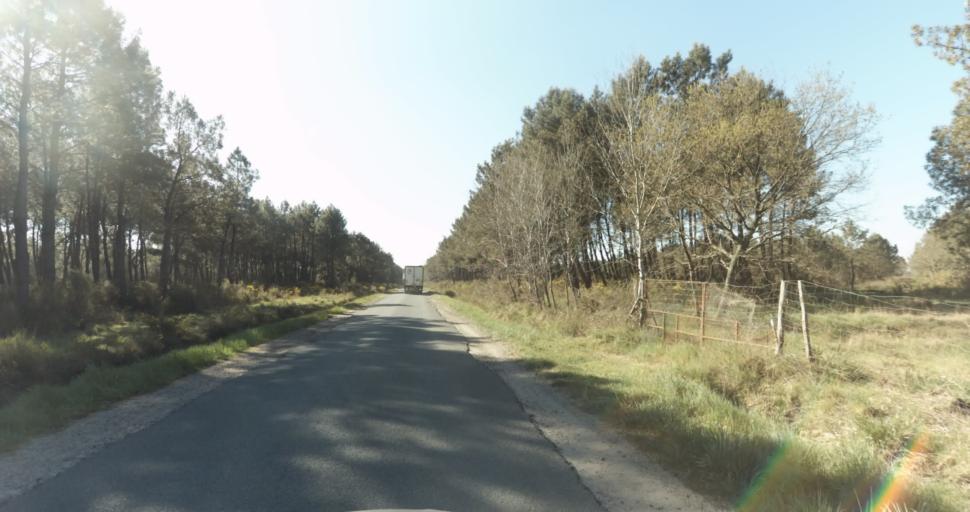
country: FR
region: Aquitaine
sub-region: Departement de la Gironde
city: Marcheprime
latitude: 44.7605
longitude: -0.8525
